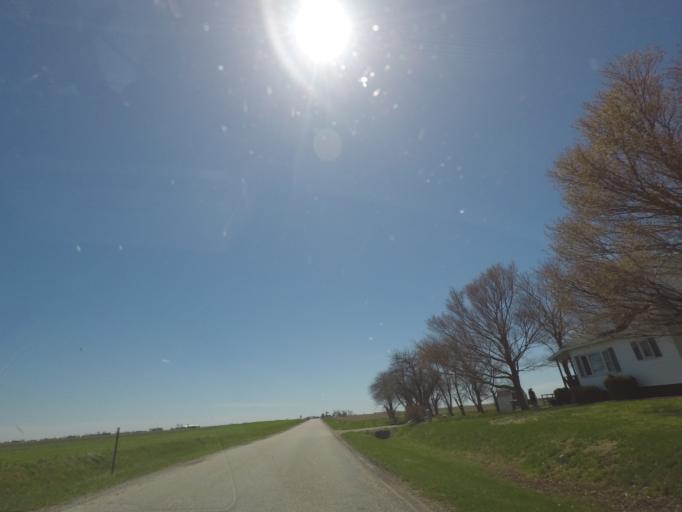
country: US
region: Illinois
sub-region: Logan County
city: Atlanta
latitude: 40.2115
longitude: -89.1944
